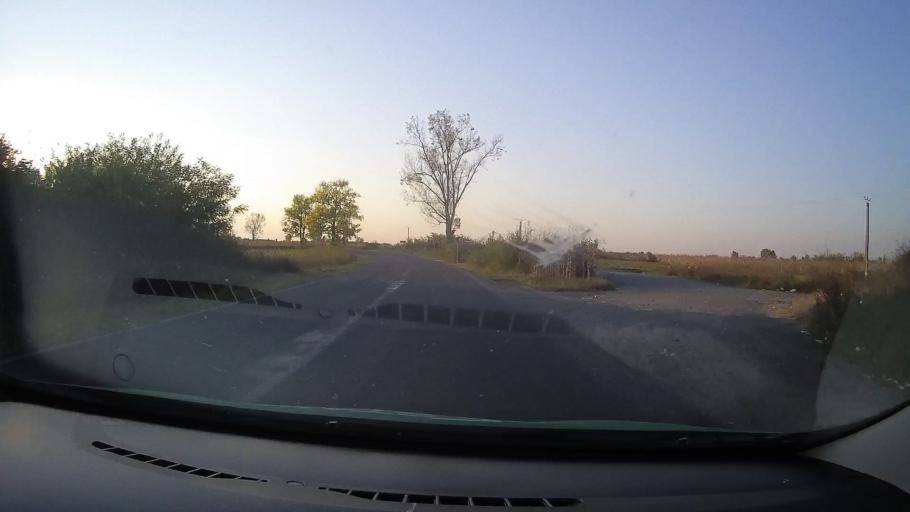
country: RO
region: Arad
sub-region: Comuna Bocsig
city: Bocsig
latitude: 46.4282
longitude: 21.9068
